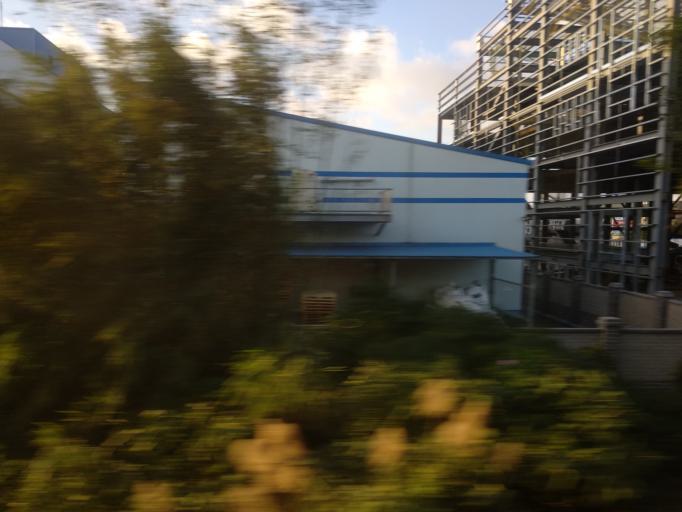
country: TW
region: Taiwan
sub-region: Hsinchu
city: Zhubei
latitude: 24.8965
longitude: 121.0391
